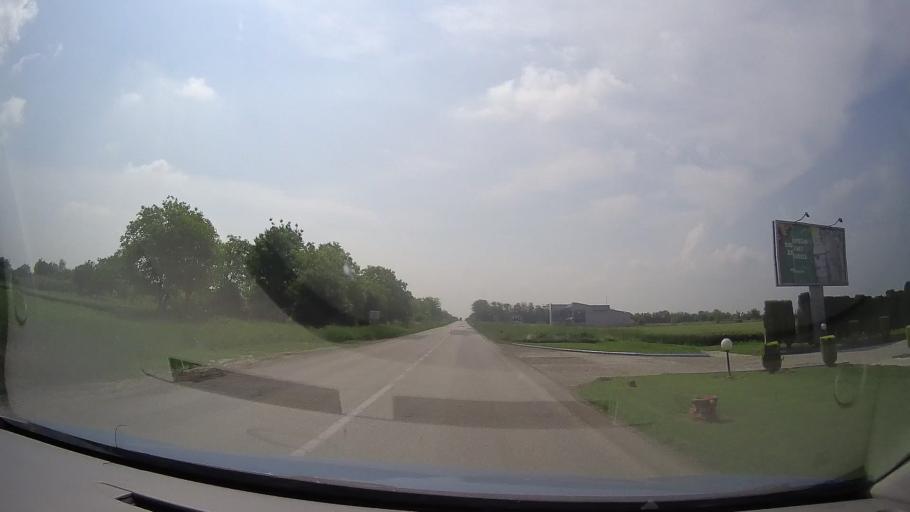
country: RS
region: Autonomna Pokrajina Vojvodina
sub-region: Juznobanatski Okrug
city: Kovacica
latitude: 45.0994
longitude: 20.6262
